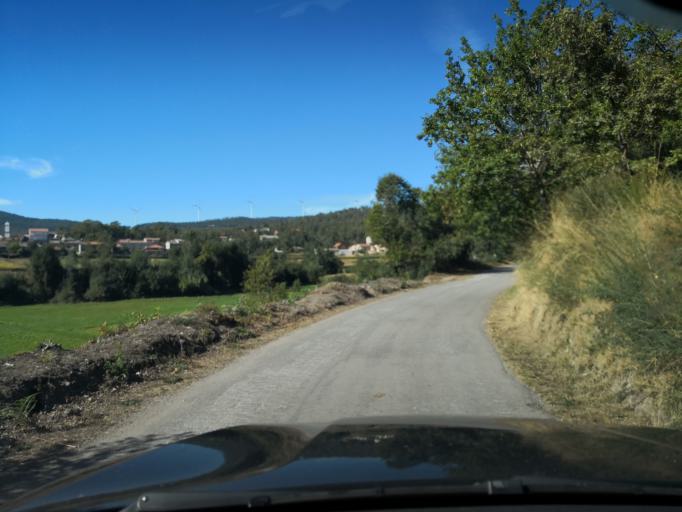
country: PT
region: Vila Real
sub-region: Santa Marta de Penaguiao
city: Santa Marta de Penaguiao
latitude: 41.2974
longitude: -7.8670
